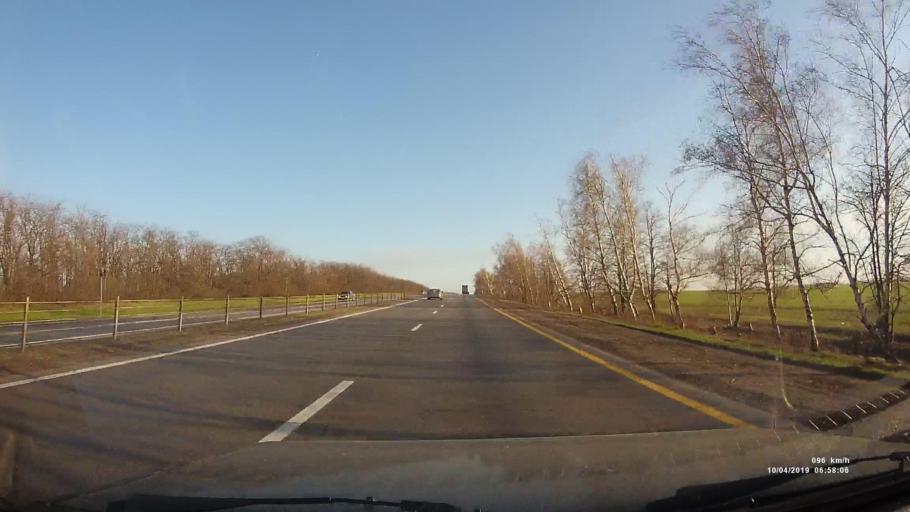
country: RU
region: Rostov
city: Grushevskaya
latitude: 47.5461
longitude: 39.9679
